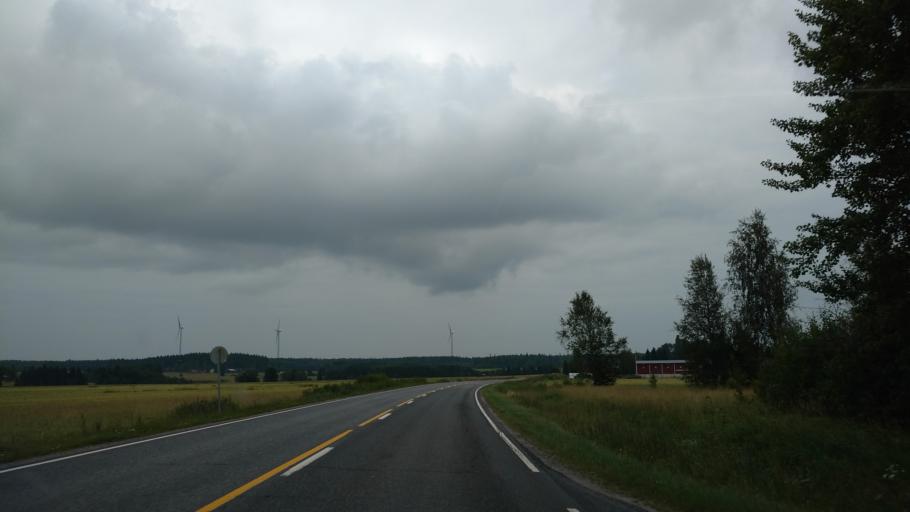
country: FI
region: Varsinais-Suomi
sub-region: Salo
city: Halikko
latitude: 60.4790
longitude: 23.0093
